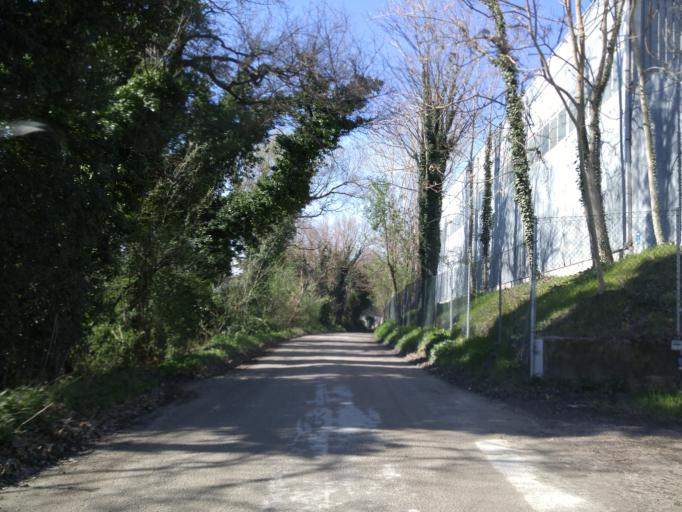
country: IT
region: The Marches
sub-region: Provincia di Pesaro e Urbino
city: Calcinelli
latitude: 43.7415
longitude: 12.9159
